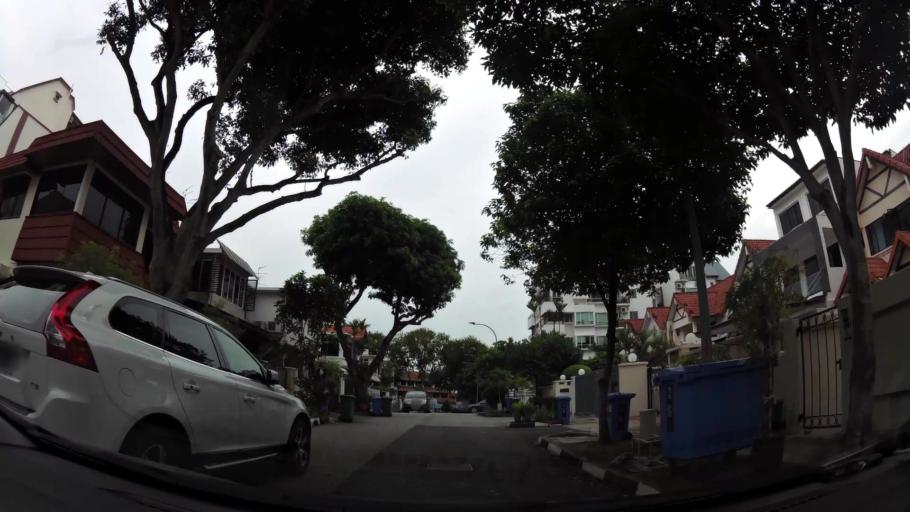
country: SG
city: Singapore
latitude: 1.3621
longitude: 103.8782
